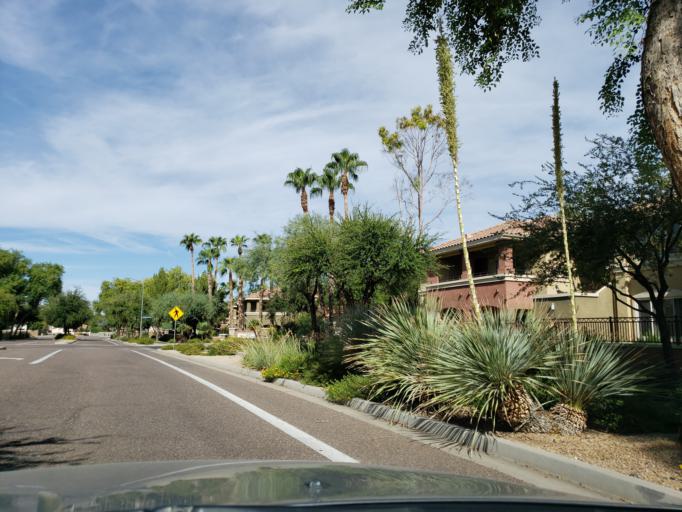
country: US
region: Arizona
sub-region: Maricopa County
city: Peoria
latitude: 33.6663
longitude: -112.1933
